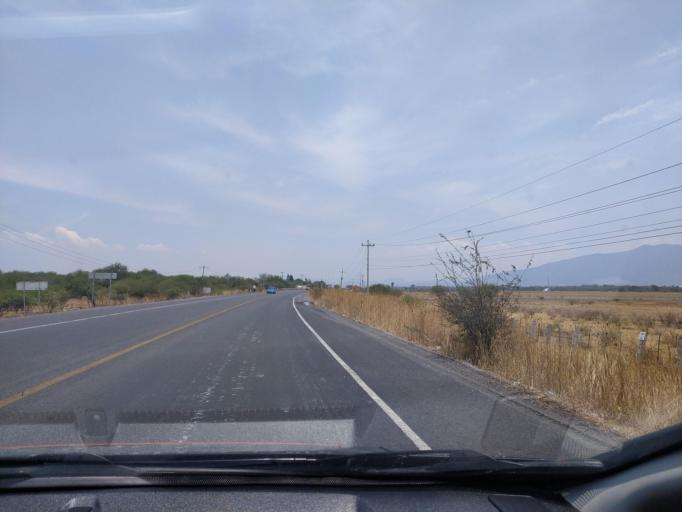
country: MX
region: Jalisco
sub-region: Zacoalco de Torres
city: Barranca de Otates (Barranca de Otatan)
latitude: 20.2923
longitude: -103.6015
